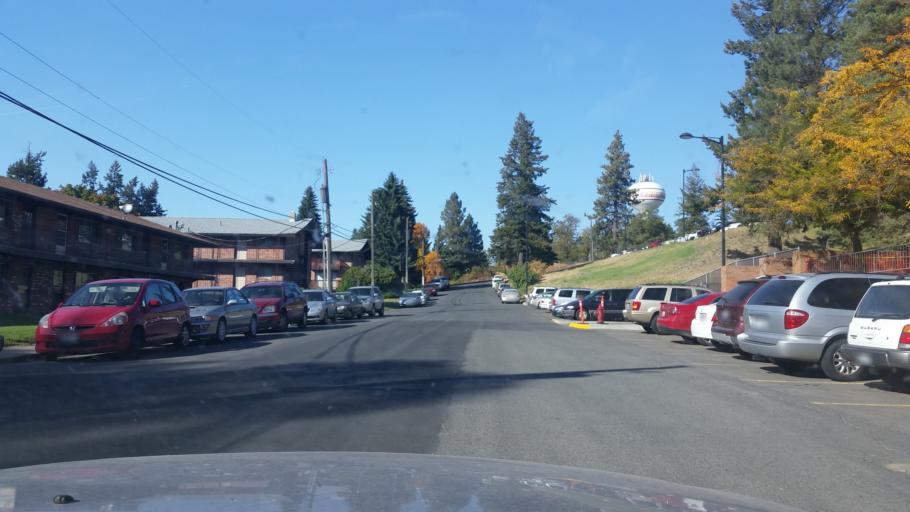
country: US
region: Washington
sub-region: Spokane County
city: Cheney
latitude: 47.4949
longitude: -117.5848
